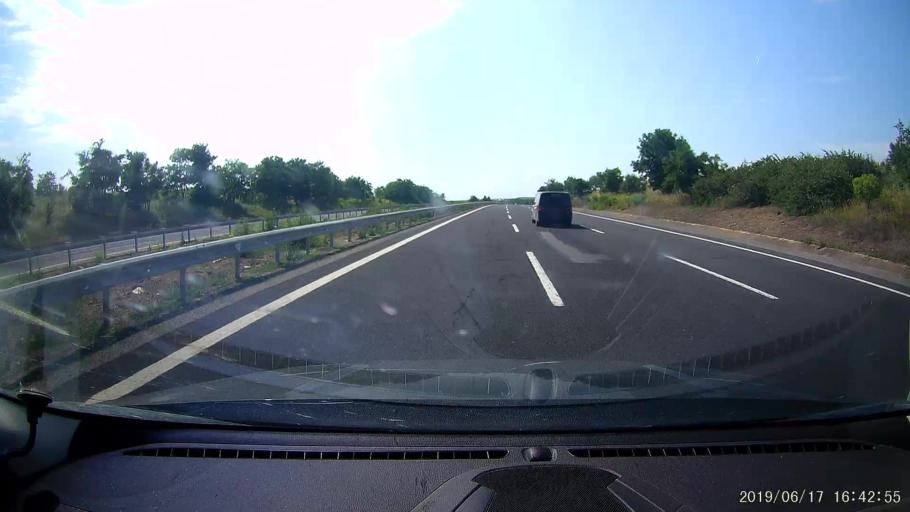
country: TR
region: Kirklareli
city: Luleburgaz
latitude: 41.4766
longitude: 27.3090
